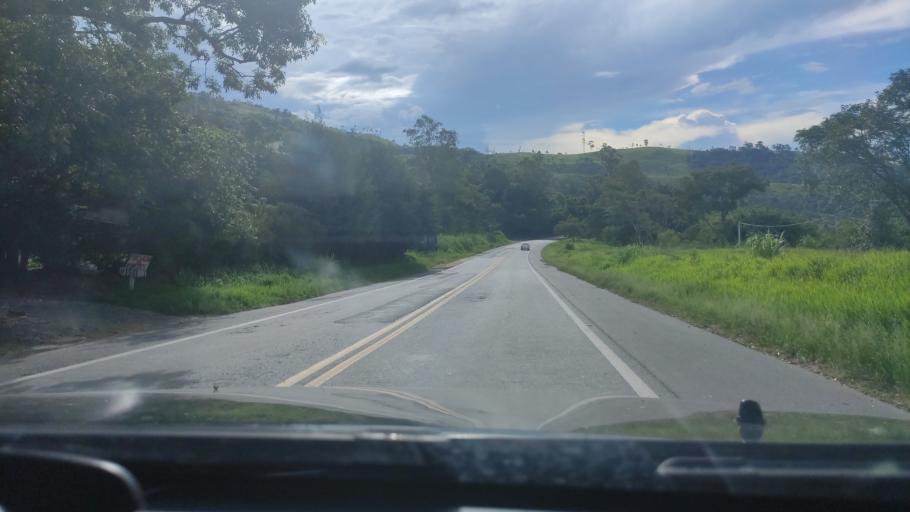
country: BR
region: Sao Paulo
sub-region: Aguas De Lindoia
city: Aguas de Lindoia
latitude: -22.5193
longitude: -46.6606
